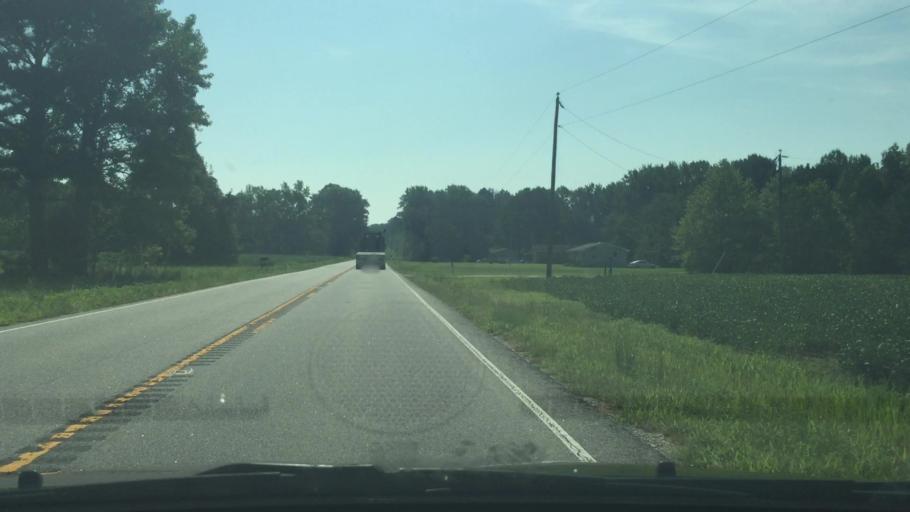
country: US
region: Virginia
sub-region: Sussex County
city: Sussex
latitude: 36.9771
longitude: -77.2125
